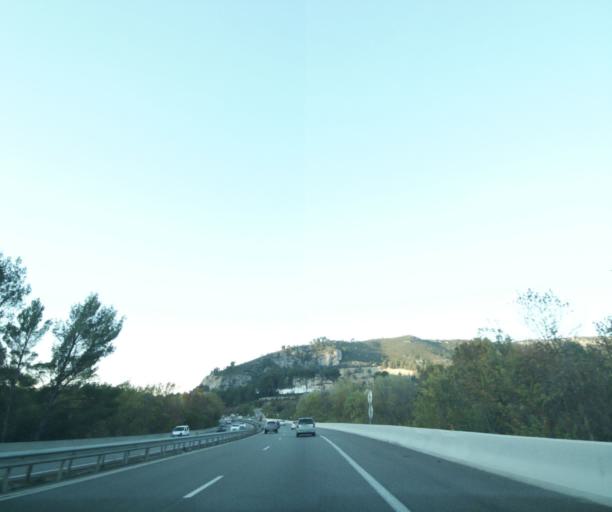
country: FR
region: Provence-Alpes-Cote d'Azur
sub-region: Departement des Bouches-du-Rhone
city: La Destrousse
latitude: 43.3637
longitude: 5.6139
